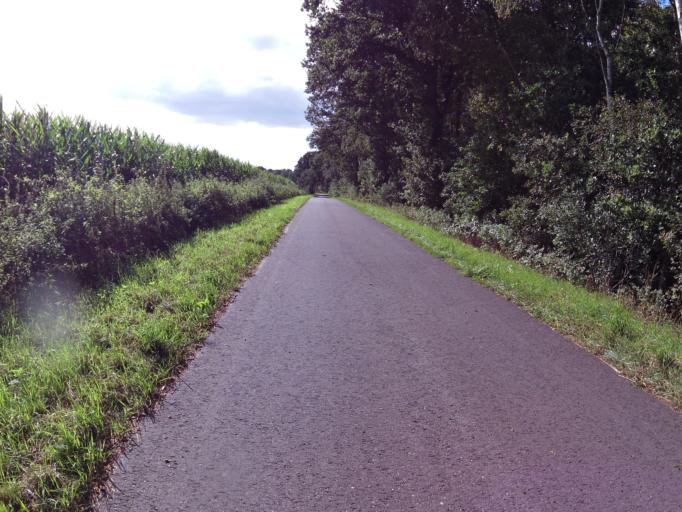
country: DE
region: Lower Saxony
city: Sandbostel
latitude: 53.4432
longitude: 9.1244
